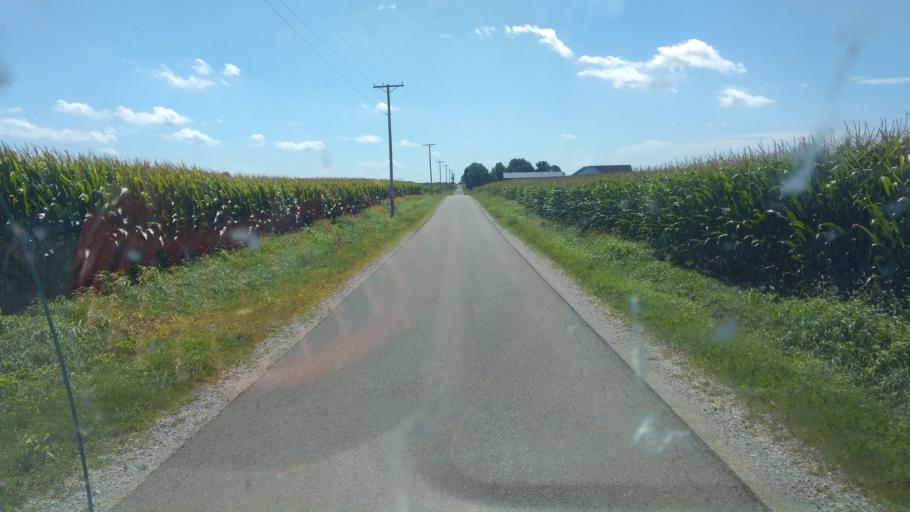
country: US
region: Ohio
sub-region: Crawford County
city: Bucyrus
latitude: 40.8185
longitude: -83.0273
